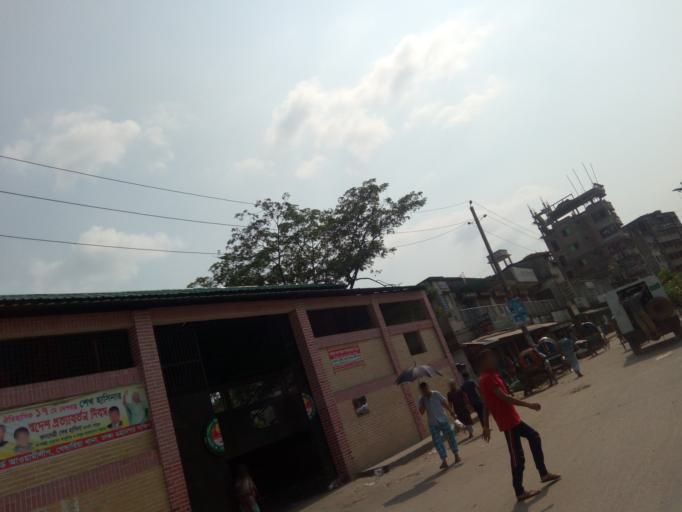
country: BD
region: Dhaka
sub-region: Dhaka
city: Dhaka
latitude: 23.7023
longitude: 90.4194
